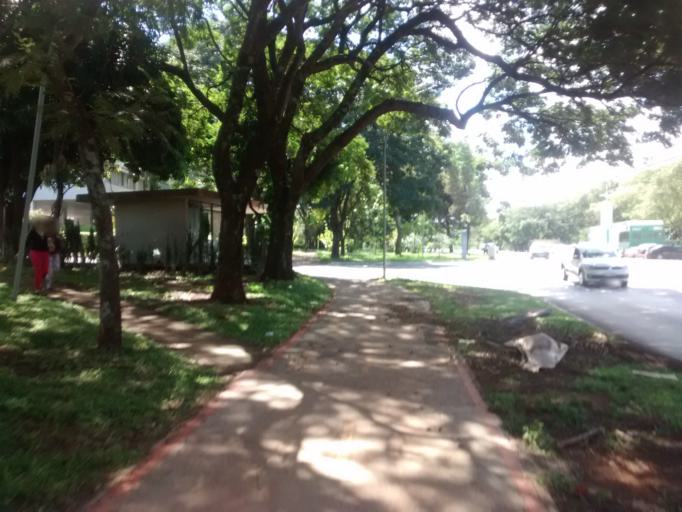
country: BR
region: Federal District
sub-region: Brasilia
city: Brasilia
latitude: -15.7770
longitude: -47.8846
